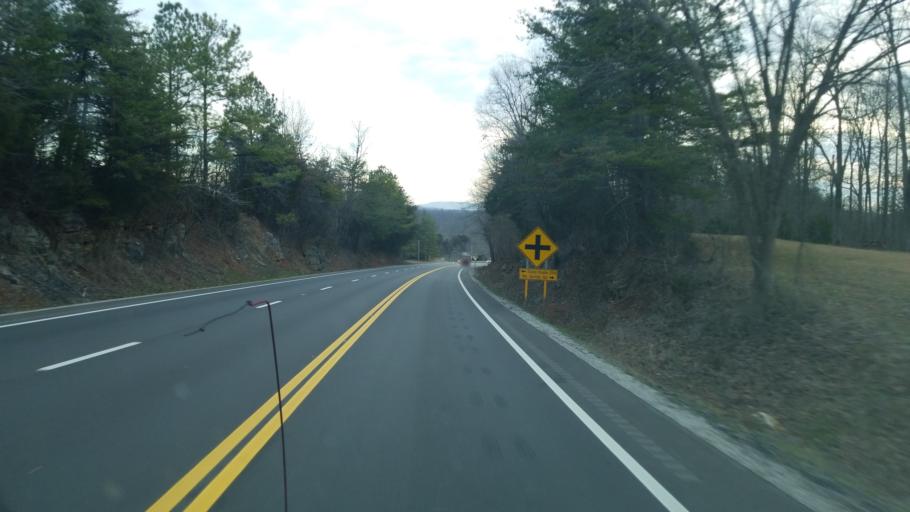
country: US
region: Tennessee
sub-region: Overton County
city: Livingston
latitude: 36.4384
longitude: -85.2711
